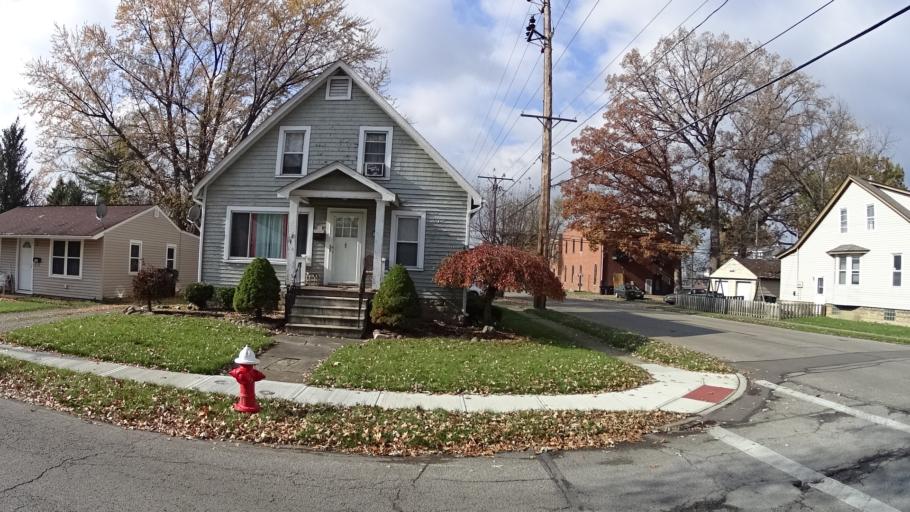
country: US
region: Ohio
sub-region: Lorain County
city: Elyria
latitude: 41.3686
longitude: -82.0861
